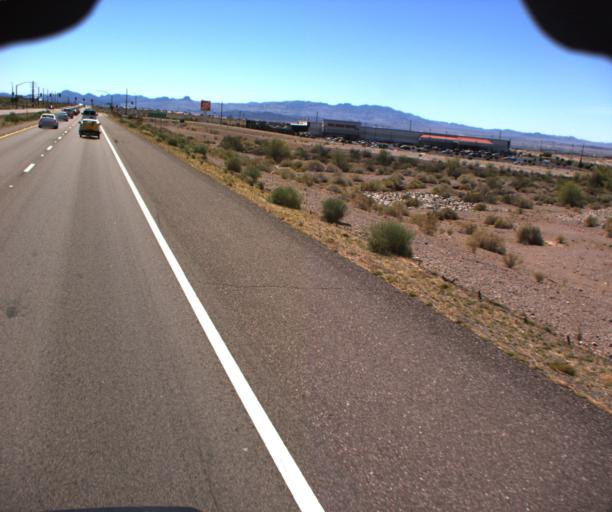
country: US
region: Arizona
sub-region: Mohave County
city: Desert Hills
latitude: 34.5655
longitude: -114.3622
